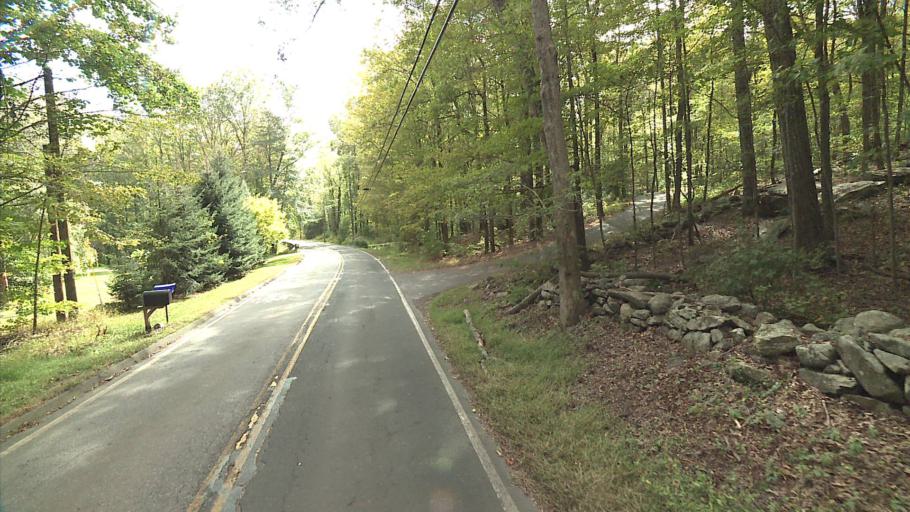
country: US
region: Connecticut
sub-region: Middlesex County
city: Higganum
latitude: 41.4062
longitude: -72.6066
